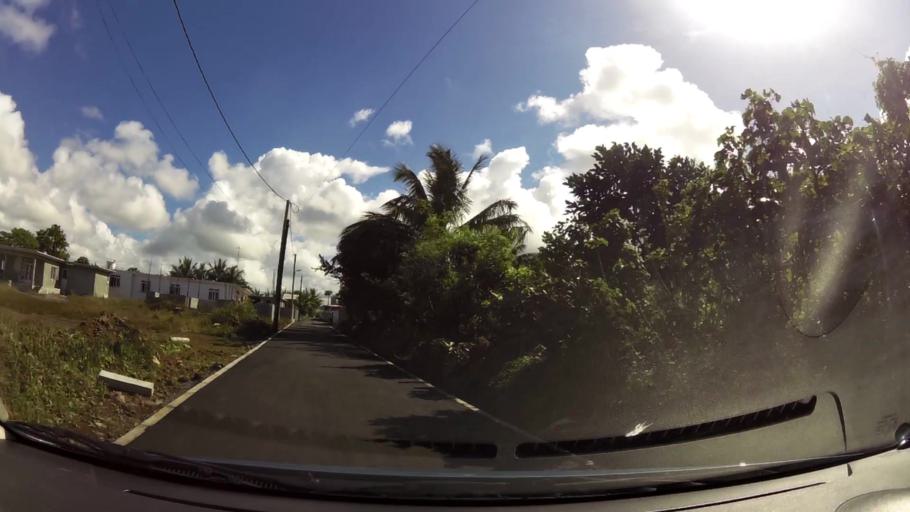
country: MU
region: Grand Port
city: Plaine Magnien
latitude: -20.4373
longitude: 57.6571
